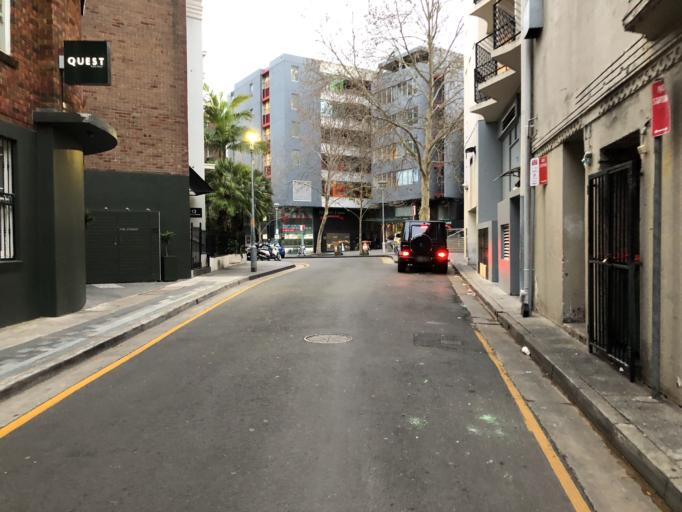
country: AU
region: New South Wales
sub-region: City of Sydney
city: Darlinghurst
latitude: -33.8734
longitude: 151.2234
